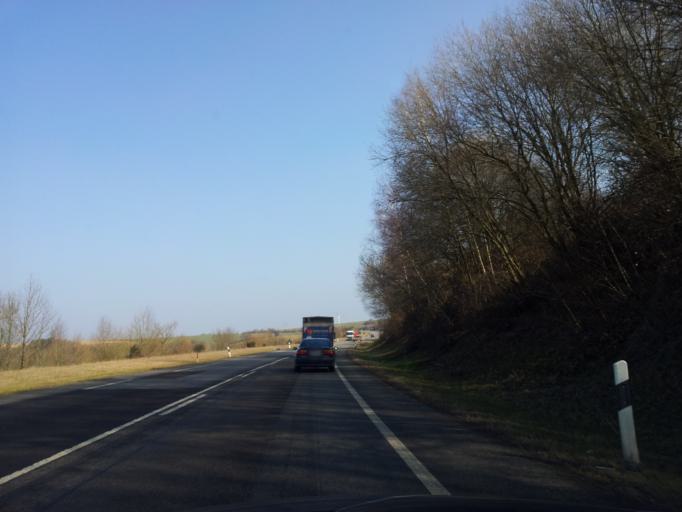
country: DE
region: Rheinland-Pfalz
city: Weselberg
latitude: 49.3415
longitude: 7.6011
